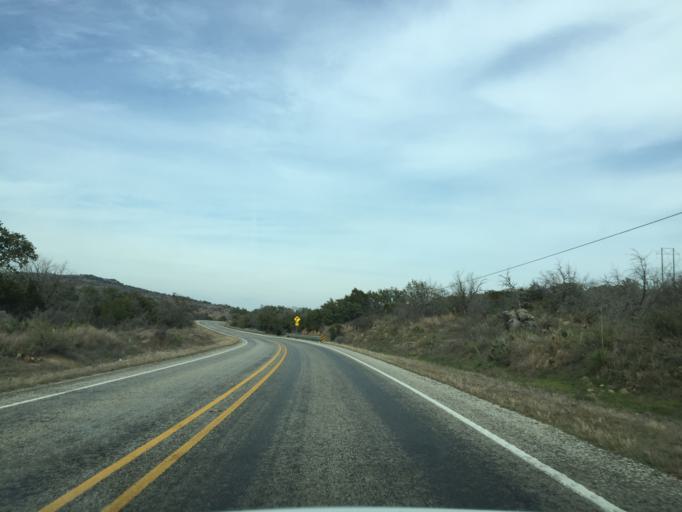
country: US
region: Texas
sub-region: Gillespie County
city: Fredericksburg
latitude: 30.4696
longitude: -98.7149
